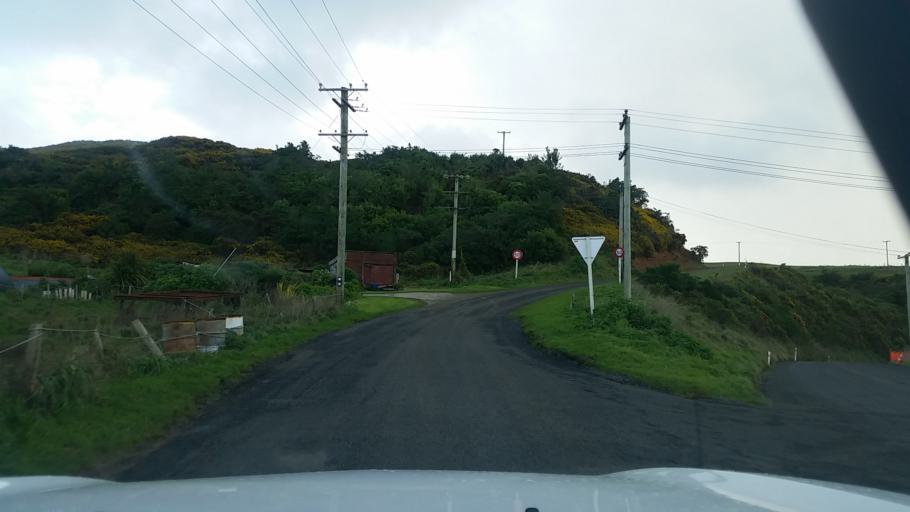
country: NZ
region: Chatham Islands
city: Waitangi
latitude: -43.9506
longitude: -176.5625
